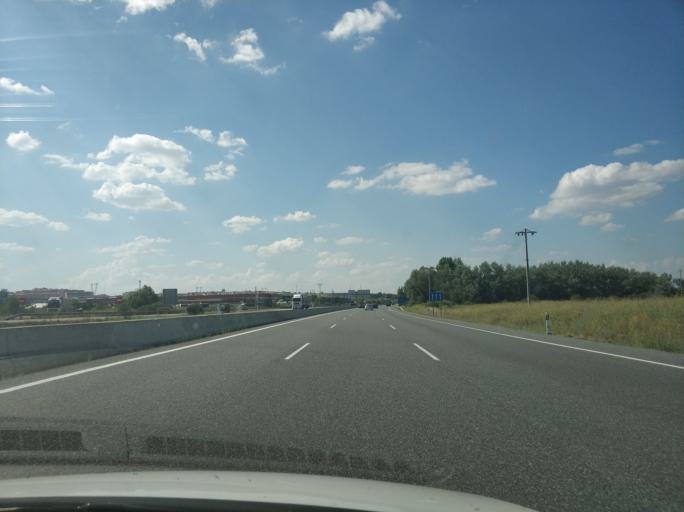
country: ES
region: Castille and Leon
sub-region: Provincia de Zamora
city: Benavente
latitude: 42.0011
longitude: -5.6575
